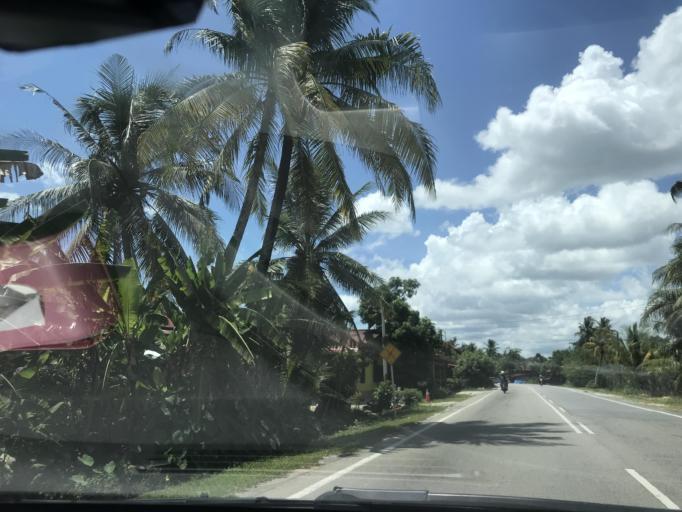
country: MY
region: Kelantan
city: Tumpat
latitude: 6.1937
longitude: 102.1433
